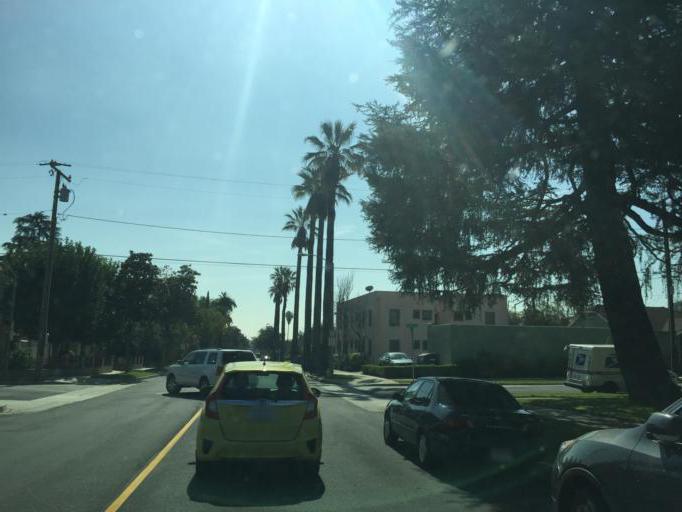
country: US
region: California
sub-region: Los Angeles County
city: Alhambra
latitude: 34.1032
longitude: -118.1204
